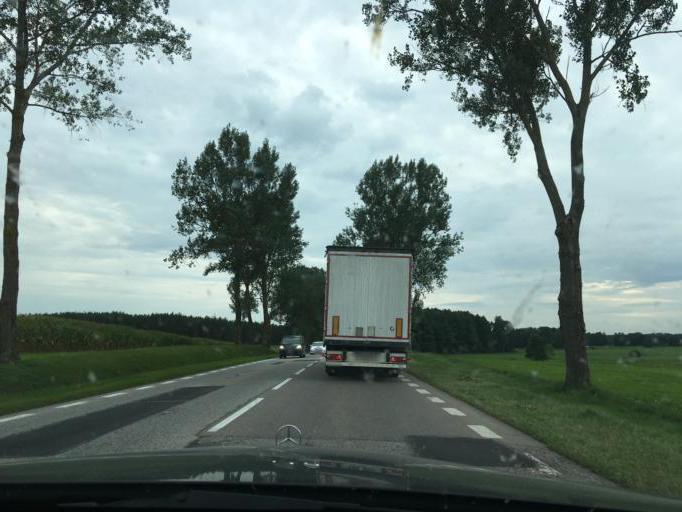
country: PL
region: Podlasie
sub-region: Powiat kolnenski
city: Stawiski
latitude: 53.3163
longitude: 22.1512
